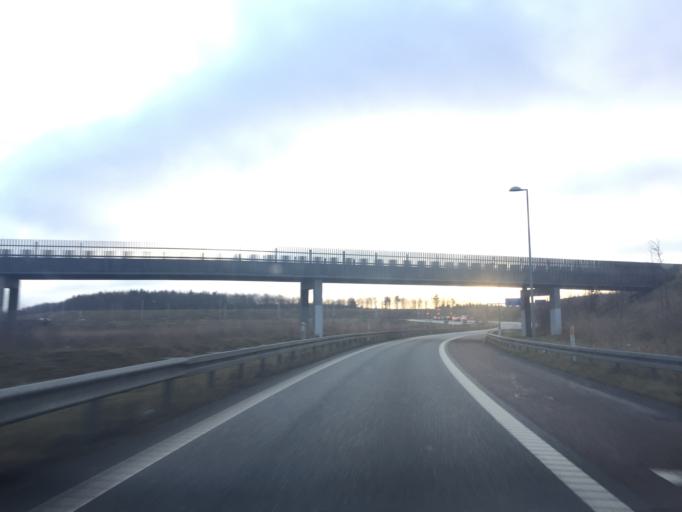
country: DK
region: Capital Region
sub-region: Glostrup Kommune
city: Glostrup
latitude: 55.6929
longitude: 12.4020
